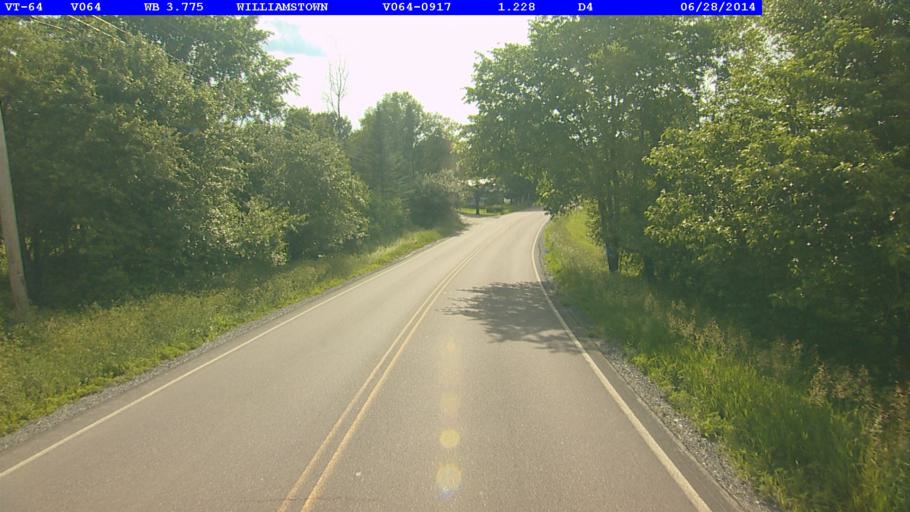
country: US
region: Vermont
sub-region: Orange County
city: Williamstown
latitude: 44.1094
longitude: -72.5912
